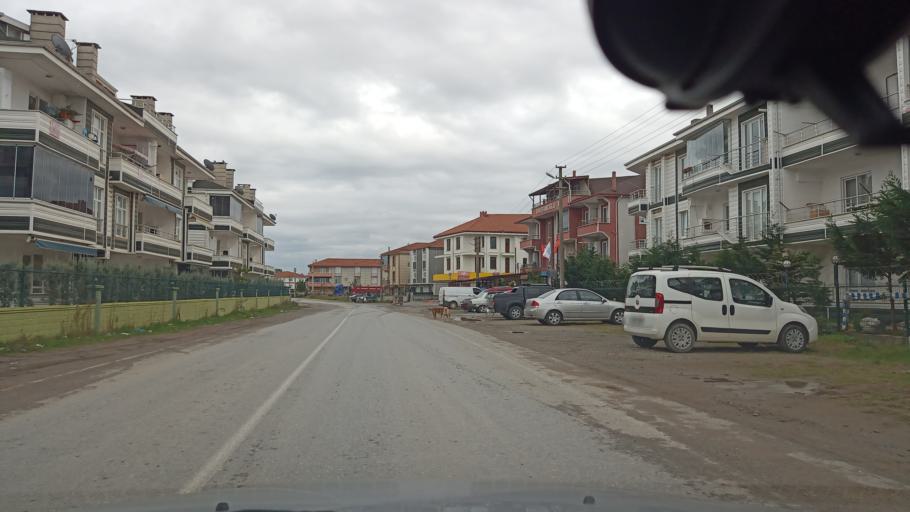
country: TR
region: Sakarya
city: Karasu
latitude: 41.1110
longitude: 30.6794
